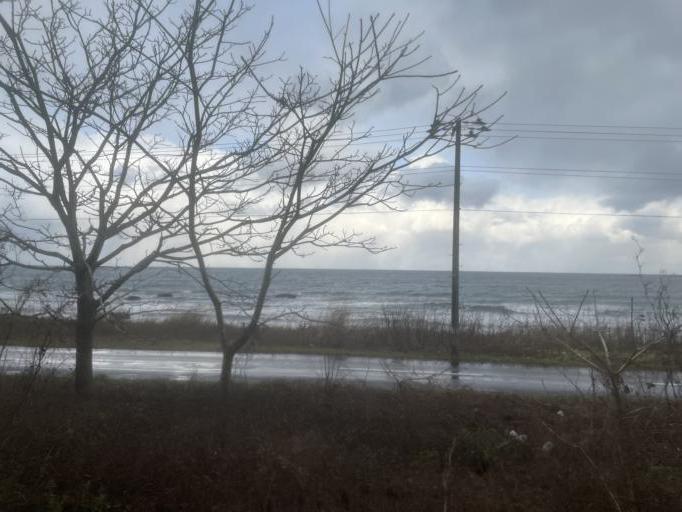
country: JP
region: Aomori
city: Shimokizukuri
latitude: 41.1880
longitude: 140.4560
